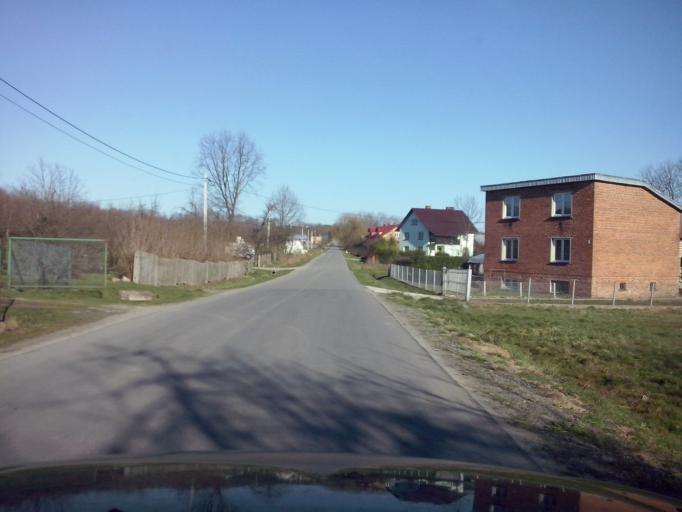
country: PL
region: Subcarpathian Voivodeship
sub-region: Powiat nizanski
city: Krzeszow
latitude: 50.3940
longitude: 22.3885
